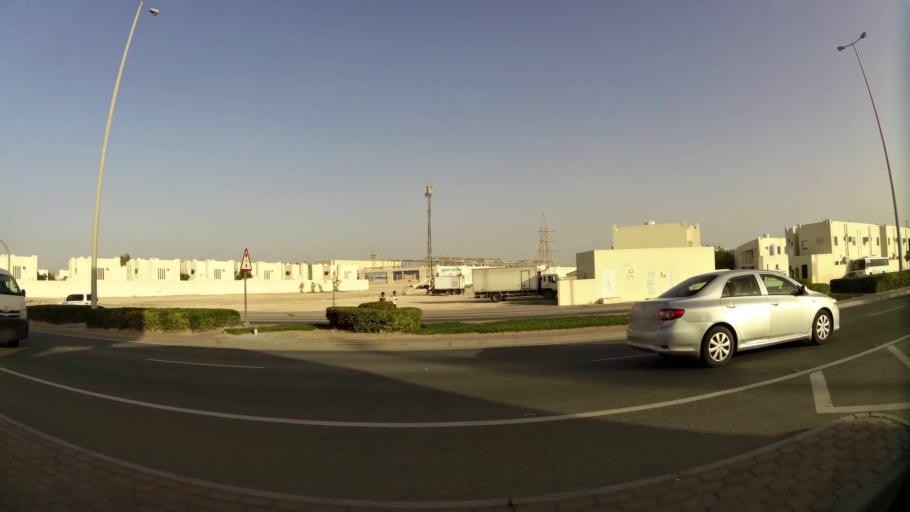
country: QA
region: Baladiyat ar Rayyan
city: Ar Rayyan
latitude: 25.3299
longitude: 51.4618
